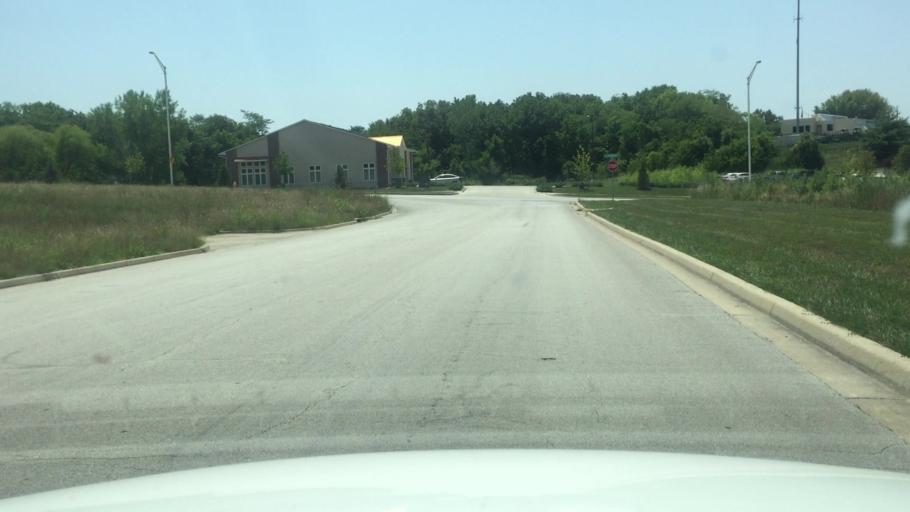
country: US
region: Missouri
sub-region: Jackson County
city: Blue Springs
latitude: 38.9861
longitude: -94.3523
